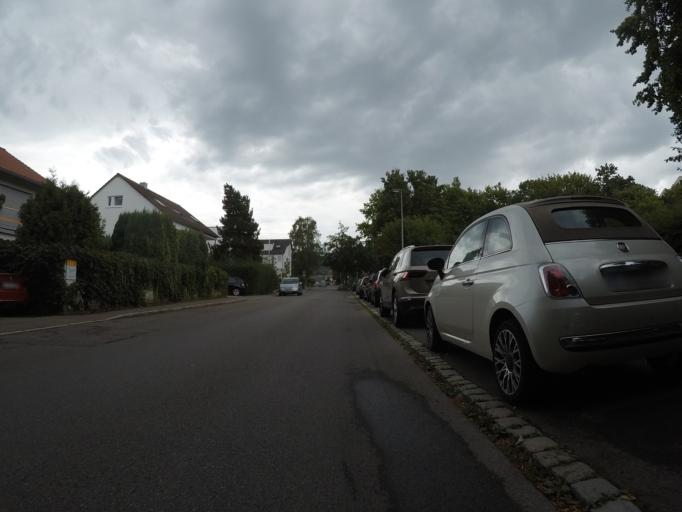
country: DE
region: Baden-Wuerttemberg
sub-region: Tuebingen Region
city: Reutlingen
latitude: 48.4866
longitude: 9.1922
